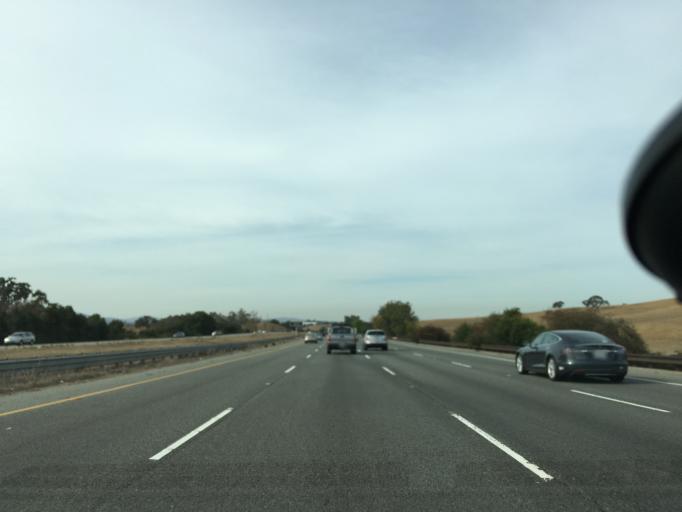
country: US
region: California
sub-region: San Mateo County
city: Ladera
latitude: 37.4004
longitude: -122.1825
